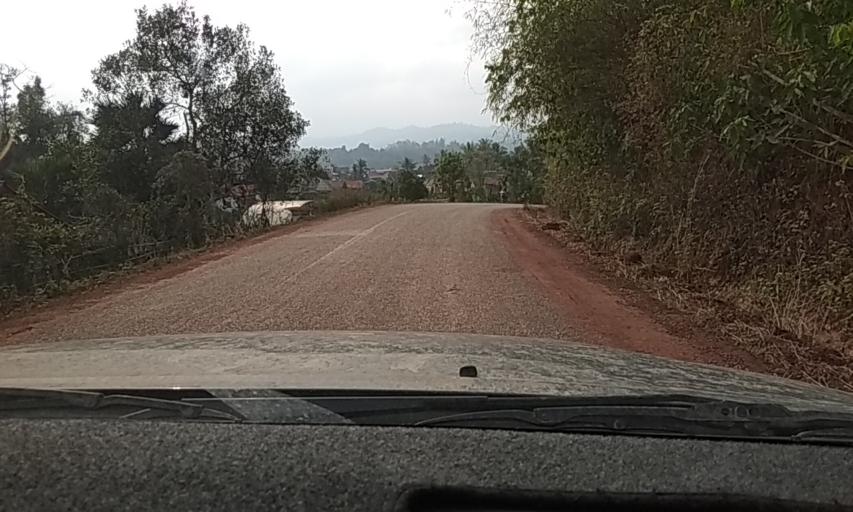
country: TH
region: Nan
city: Mae Charim
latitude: 18.4036
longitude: 101.1753
